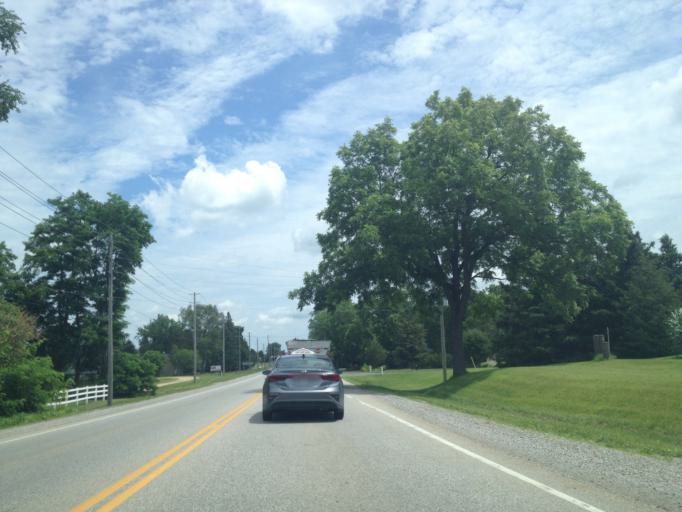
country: CA
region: Ontario
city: Norfolk County
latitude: 42.8383
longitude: -80.3474
